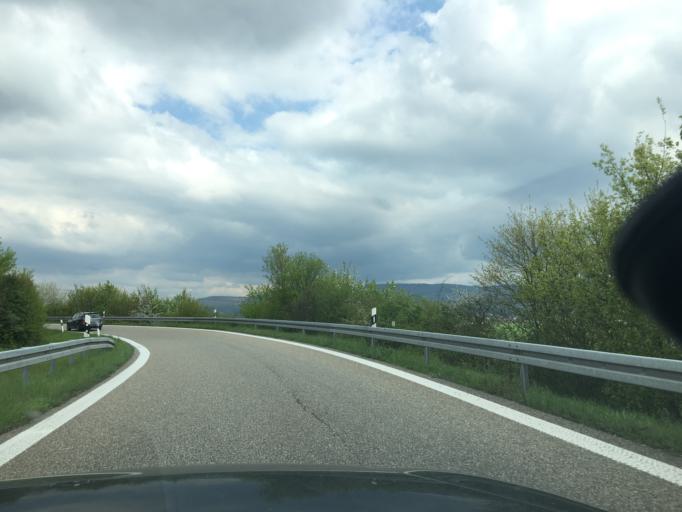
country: DE
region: Baden-Wuerttemberg
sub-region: Karlsruhe Region
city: Eppelheim
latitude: 49.3697
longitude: 8.6350
